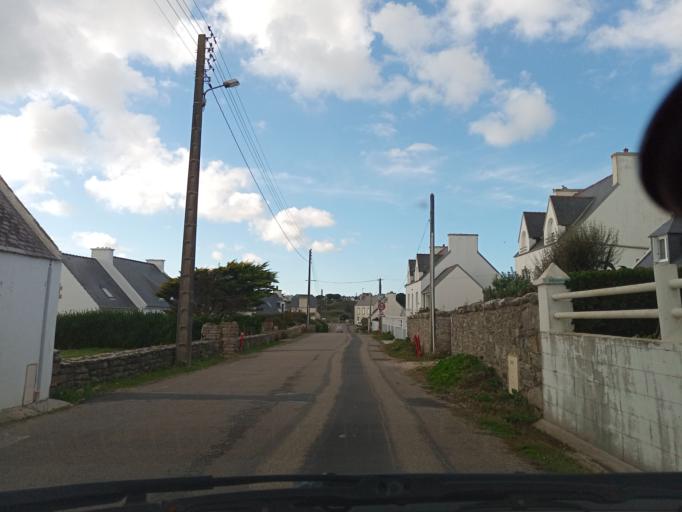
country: FR
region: Brittany
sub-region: Departement du Finistere
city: Plouhinec
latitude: 47.9843
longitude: -4.4596
